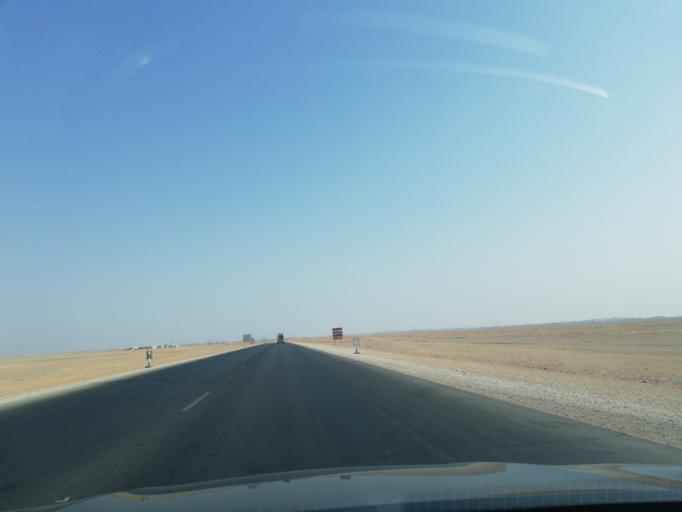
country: OM
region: Zufar
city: Salalah
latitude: 17.7289
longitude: 54.0224
